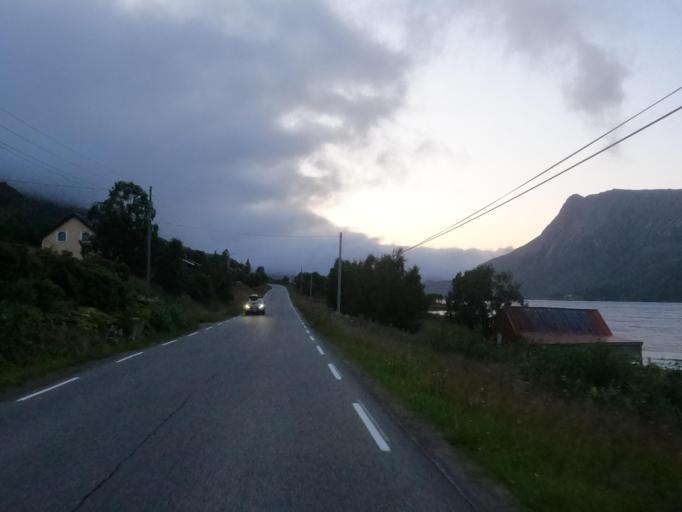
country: NO
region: Nordland
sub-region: Lodingen
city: Lodingen
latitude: 68.5726
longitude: 15.7956
